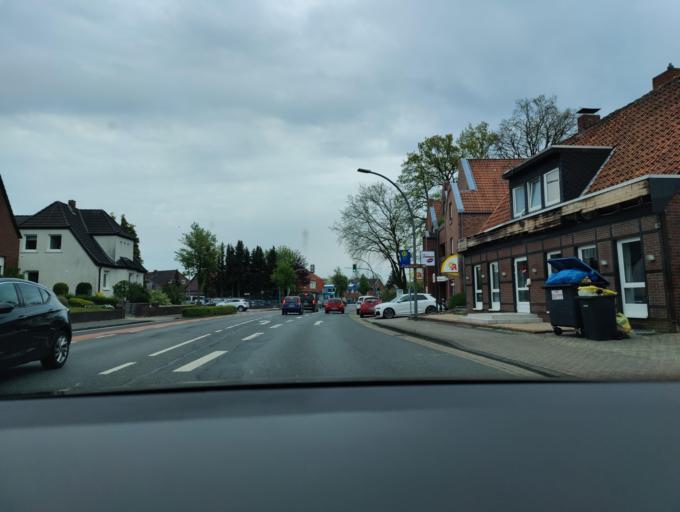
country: DE
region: Lower Saxony
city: Lingen
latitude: 52.5320
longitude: 7.3078
